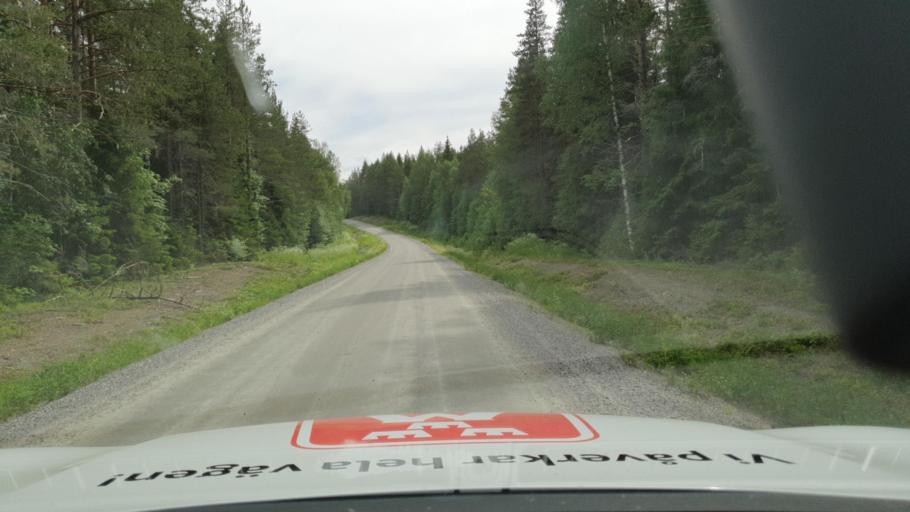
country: SE
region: Vaesterbotten
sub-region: Skelleftea Kommun
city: Burea
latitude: 64.4416
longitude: 21.0183
